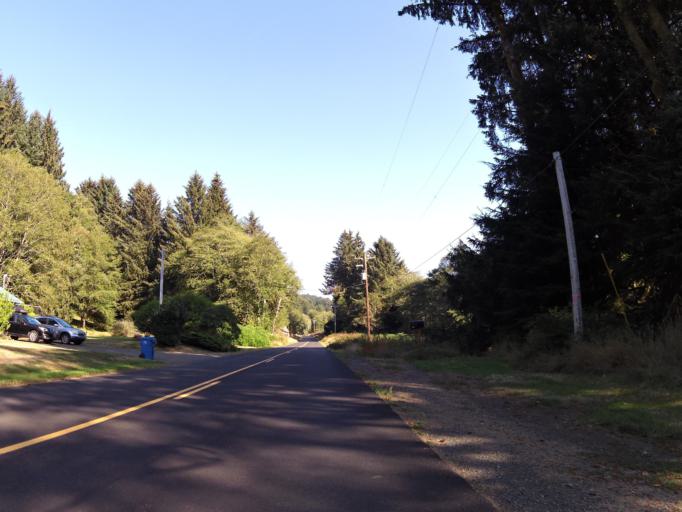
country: US
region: Oregon
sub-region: Lincoln County
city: Rose Lodge
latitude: 45.0756
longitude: -123.9341
